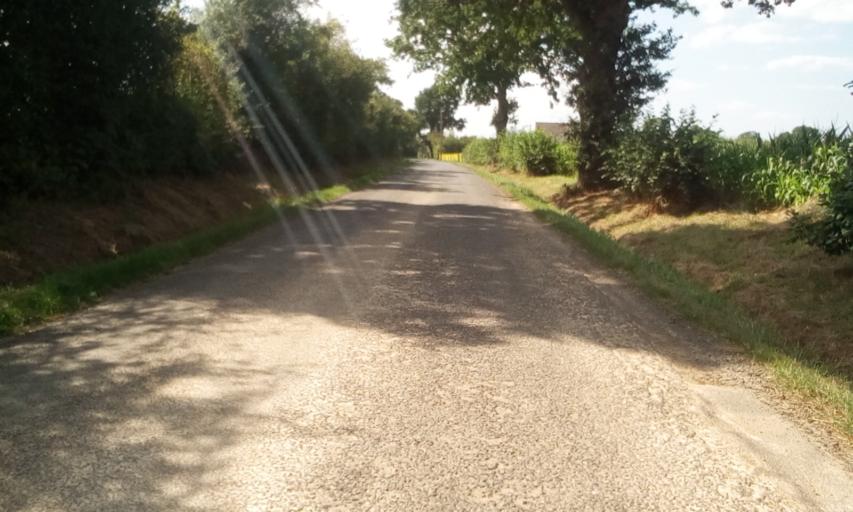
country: FR
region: Lower Normandy
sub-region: Departement du Calvados
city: Argences
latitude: 49.1535
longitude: -0.1399
